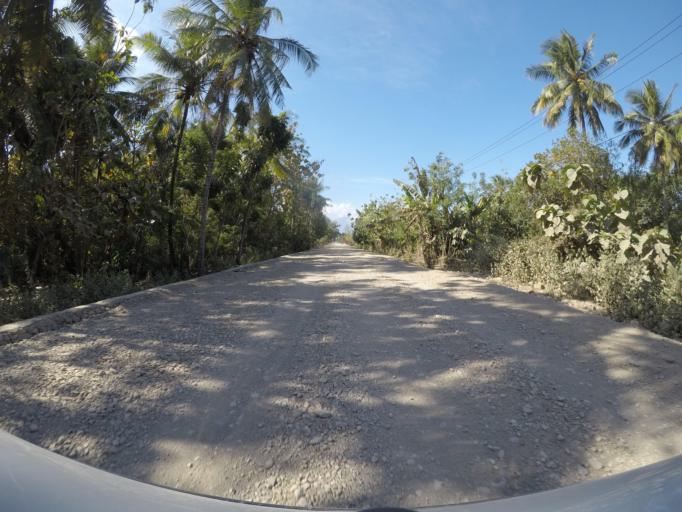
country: TL
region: Viqueque
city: Viqueque
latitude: -8.8558
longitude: 126.5109
